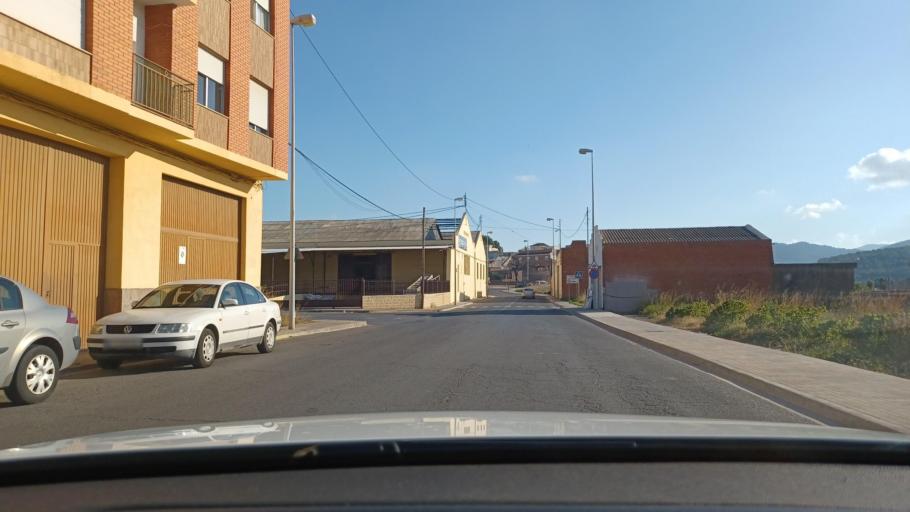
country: ES
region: Valencia
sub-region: Provincia de Castello
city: Onda
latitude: 39.9642
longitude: -0.2518
